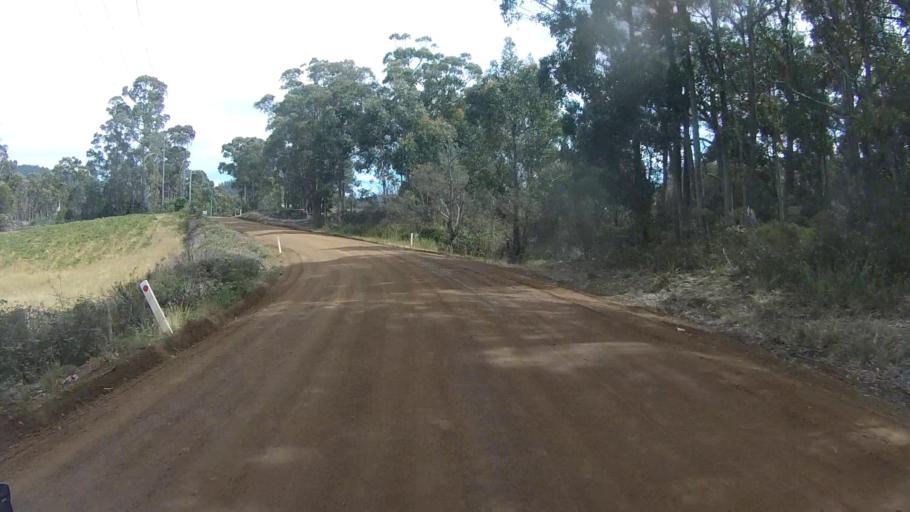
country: AU
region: Tasmania
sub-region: Sorell
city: Sorell
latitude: -42.7786
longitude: 147.8100
